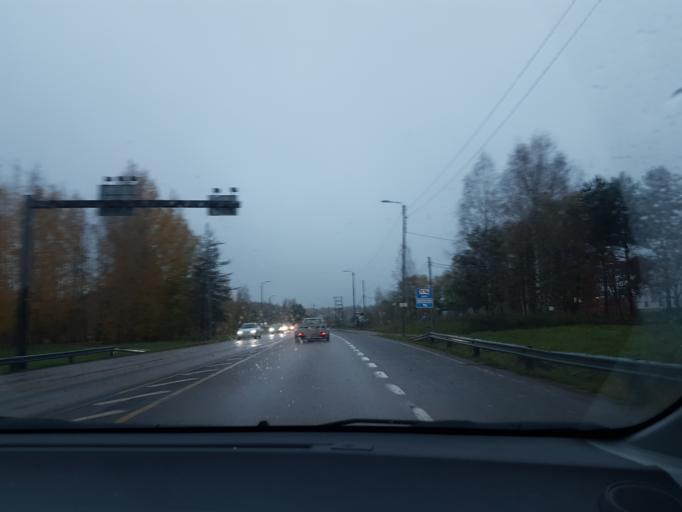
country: FI
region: Uusimaa
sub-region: Helsinki
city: Tuusula
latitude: 60.4148
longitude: 25.0510
